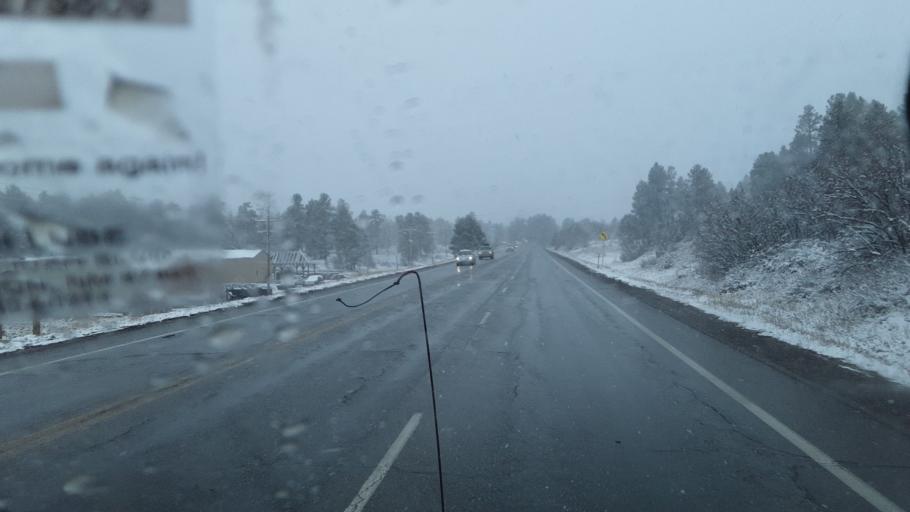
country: US
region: Colorado
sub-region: Archuleta County
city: Pagosa Springs
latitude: 37.2700
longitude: -107.0308
